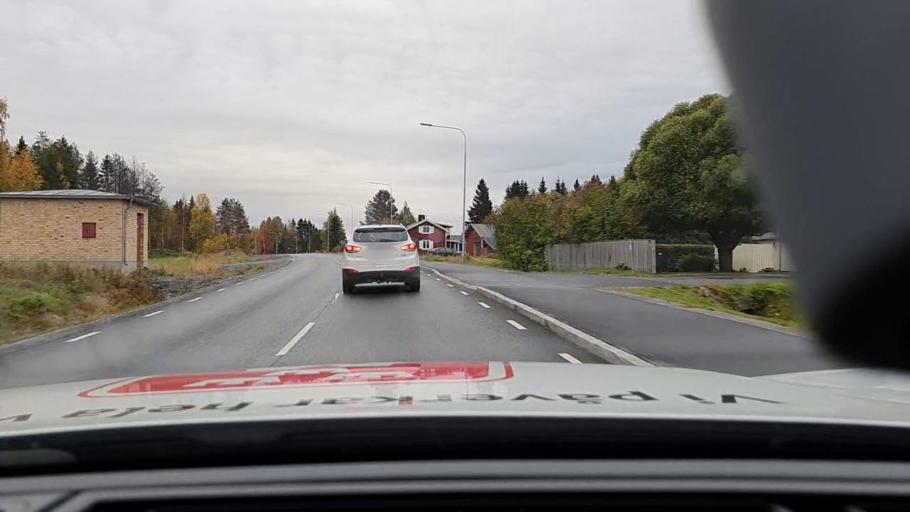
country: SE
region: Norrbotten
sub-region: Bodens Kommun
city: Saevast
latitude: 65.7750
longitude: 21.6951
